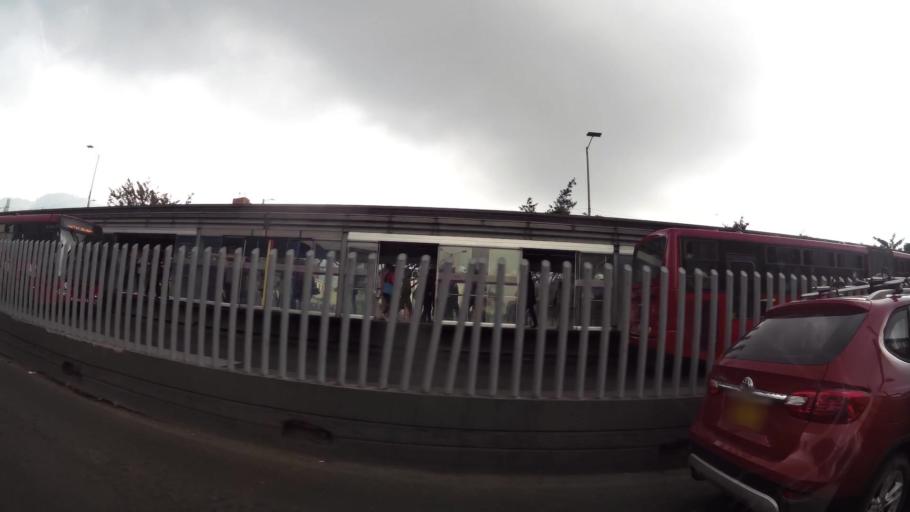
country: CO
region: Bogota D.C.
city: Bogota
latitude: 4.5982
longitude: -74.0839
